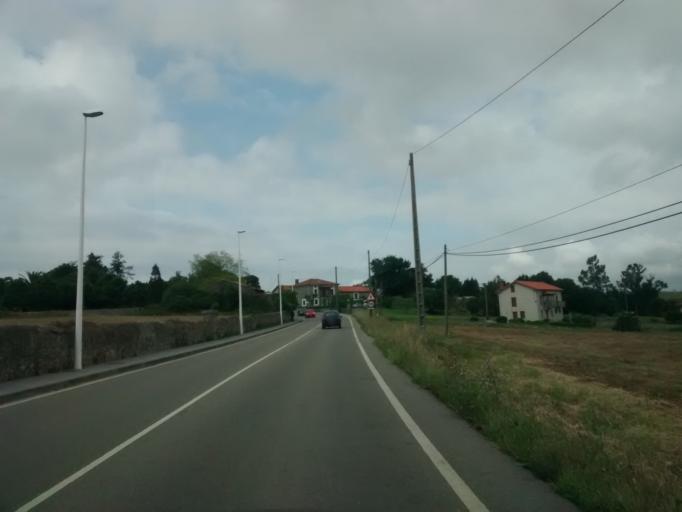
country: ES
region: Cantabria
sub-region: Provincia de Cantabria
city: Santander
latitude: 43.4330
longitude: -3.7726
